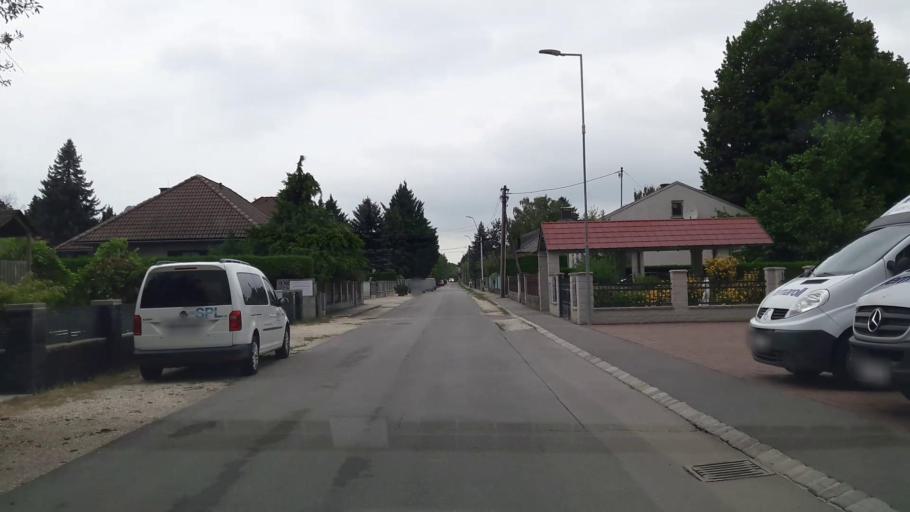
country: AT
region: Lower Austria
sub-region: Politischer Bezirk Ganserndorf
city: Strasshof an der Nordbahn
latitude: 48.3230
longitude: 16.6769
